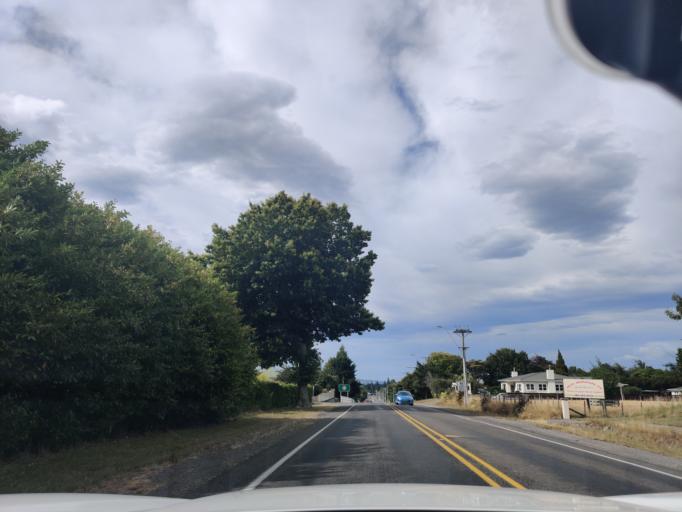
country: NZ
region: Wellington
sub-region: Masterton District
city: Masterton
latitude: -40.9358
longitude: 175.6711
